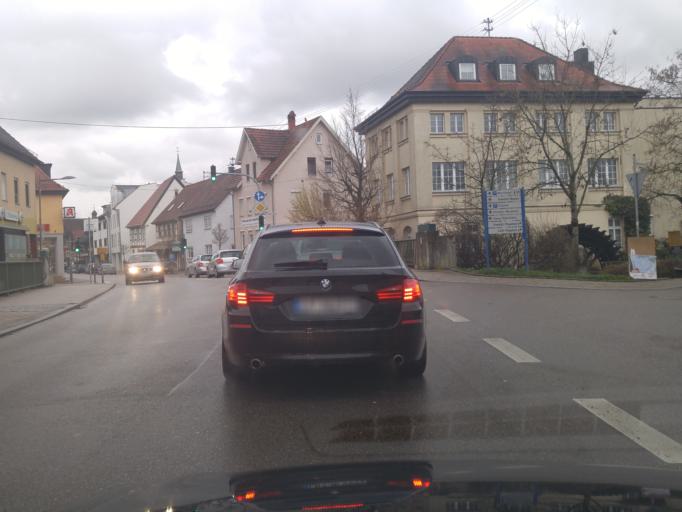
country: DE
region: Baden-Wuerttemberg
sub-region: Regierungsbezirk Stuttgart
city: Steinheim am der Murr
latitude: 48.9665
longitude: 9.2768
